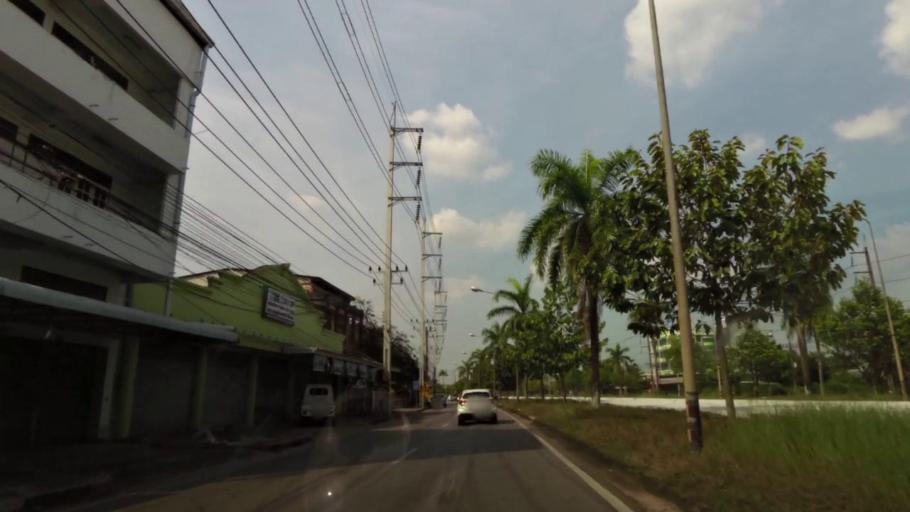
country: TH
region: Rayong
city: Klaeng
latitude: 12.7881
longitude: 101.6491
